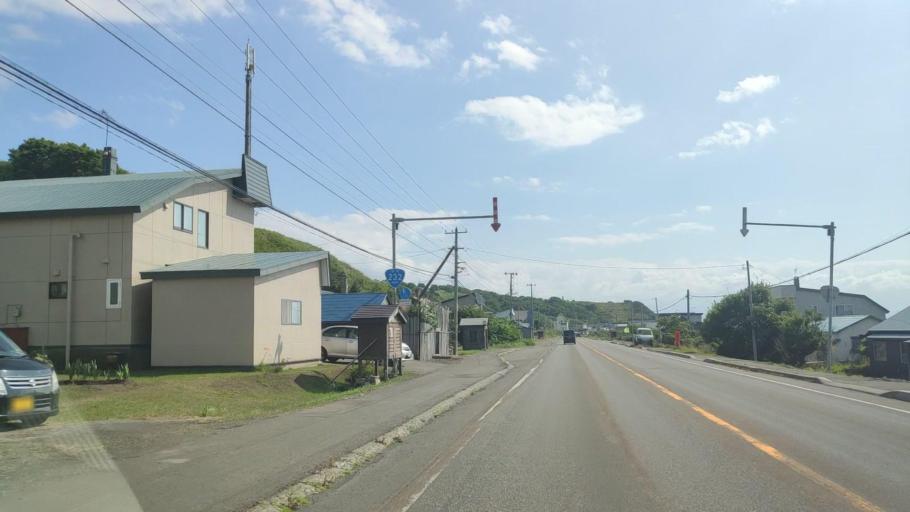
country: JP
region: Hokkaido
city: Rumoi
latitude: 43.9696
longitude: 141.6467
